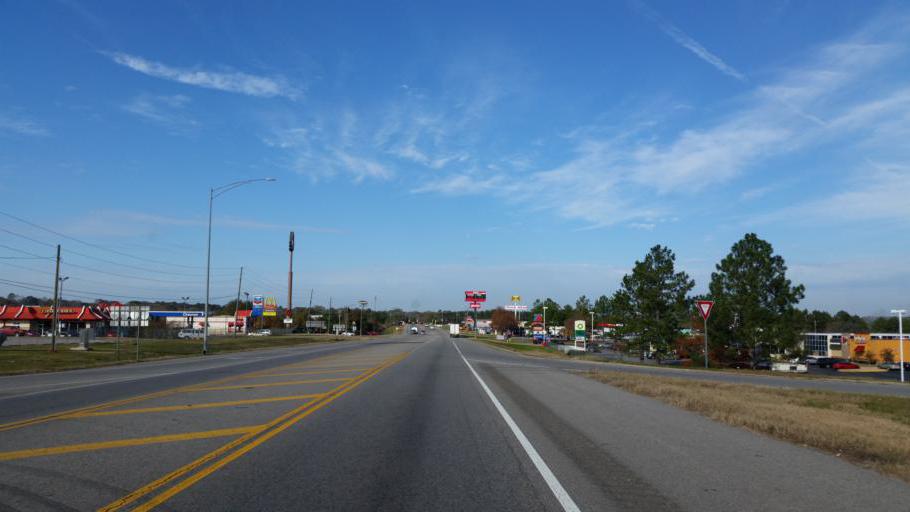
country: US
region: Alabama
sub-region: Tuscaloosa County
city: Holt
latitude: 33.1744
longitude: -87.4474
